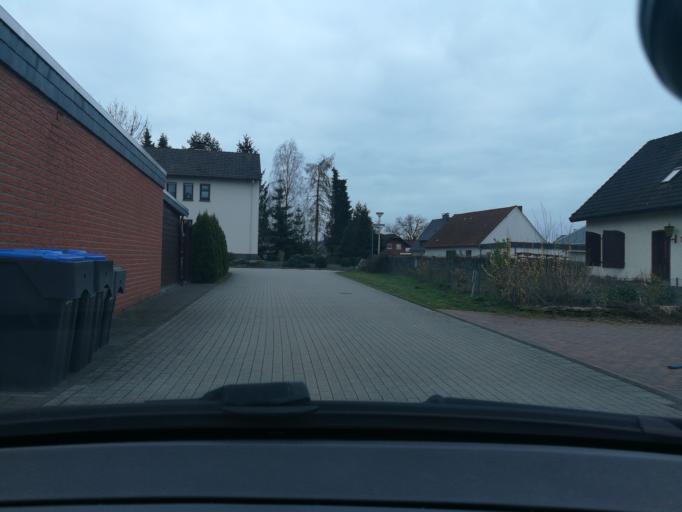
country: DE
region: North Rhine-Westphalia
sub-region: Regierungsbezirk Detmold
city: Oerlinghausen
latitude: 51.9379
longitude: 8.6343
